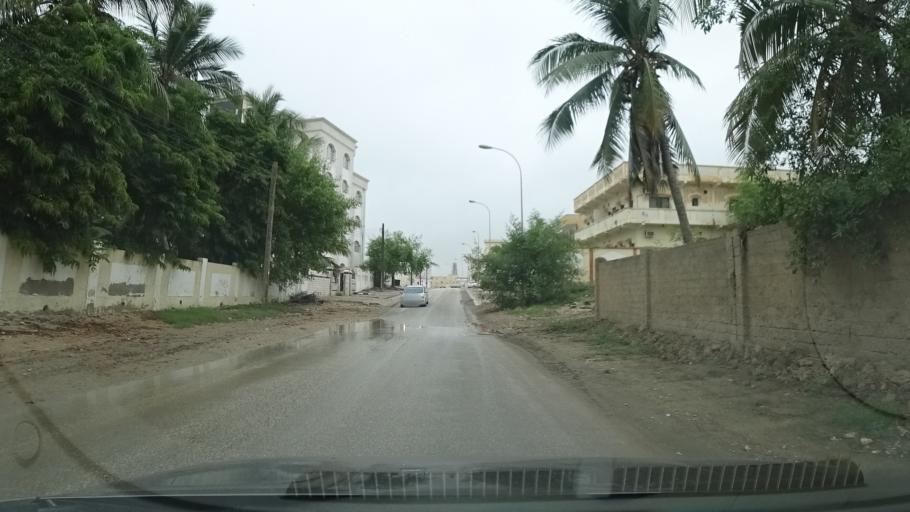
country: OM
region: Zufar
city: Salalah
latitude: 17.0179
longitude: 54.0715
